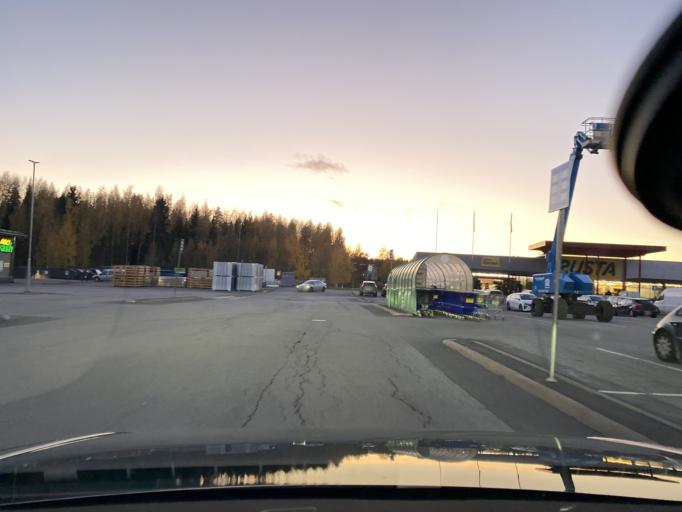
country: FI
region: Pirkanmaa
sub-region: Tampere
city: Tampere
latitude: 61.4685
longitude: 23.7165
